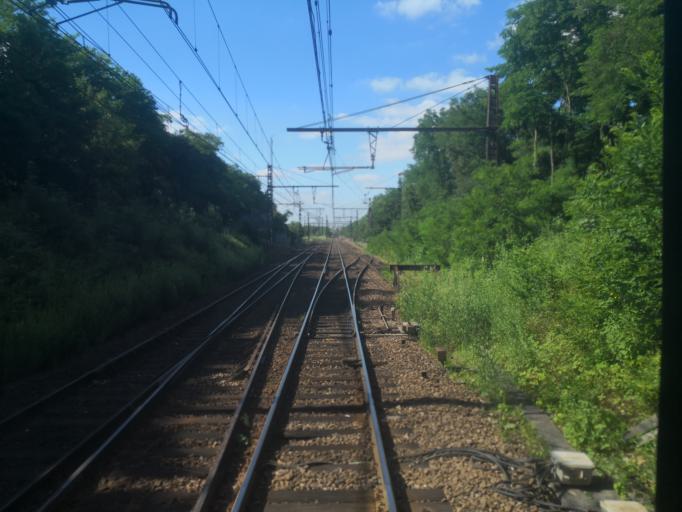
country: FR
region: Ile-de-France
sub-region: Departement de Seine-et-Marne
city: La Rochette
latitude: 48.5156
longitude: 2.6665
